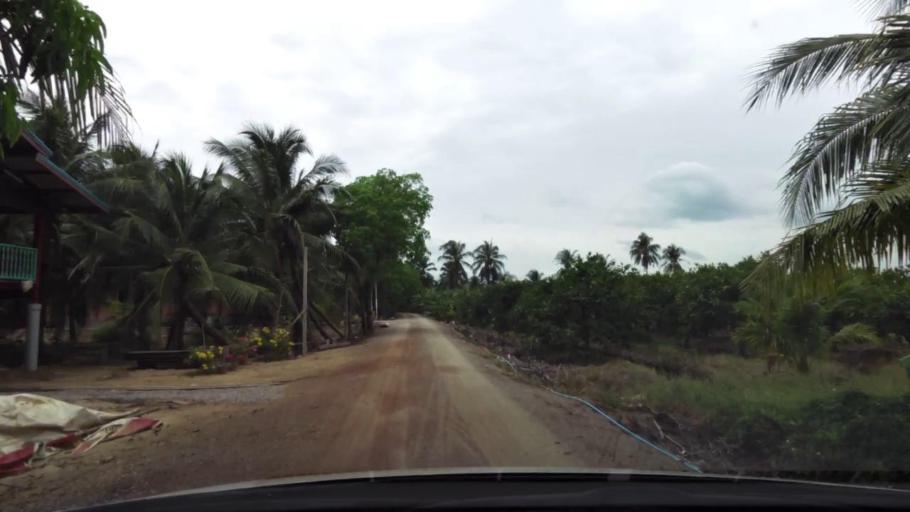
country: TH
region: Ratchaburi
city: Damnoen Saduak
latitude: 13.5556
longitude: 99.9930
